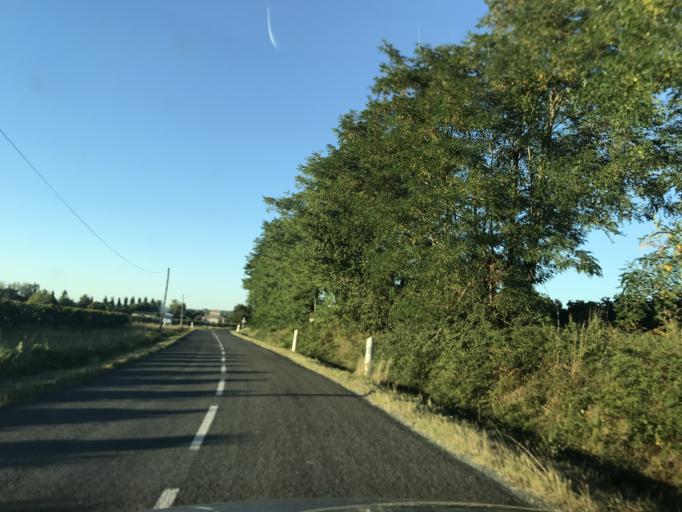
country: FR
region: Aquitaine
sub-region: Departement de la Gironde
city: Saint-Medard-de-Guizieres
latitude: 45.0004
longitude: -0.0541
